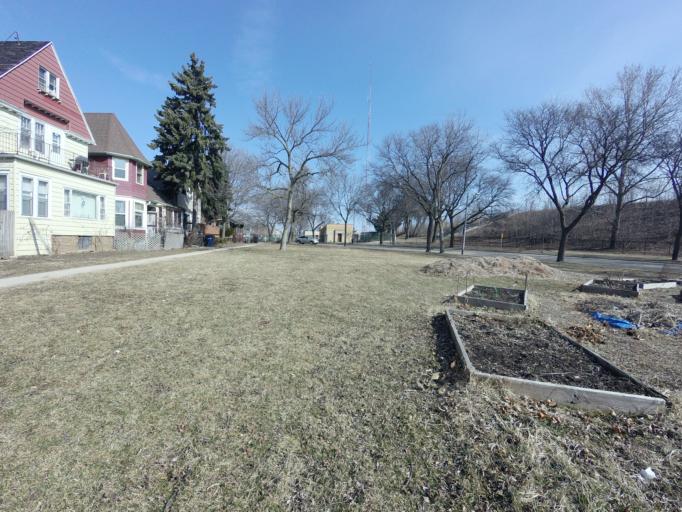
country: US
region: Wisconsin
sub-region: Milwaukee County
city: Milwaukee
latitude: 43.0596
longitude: -87.9033
